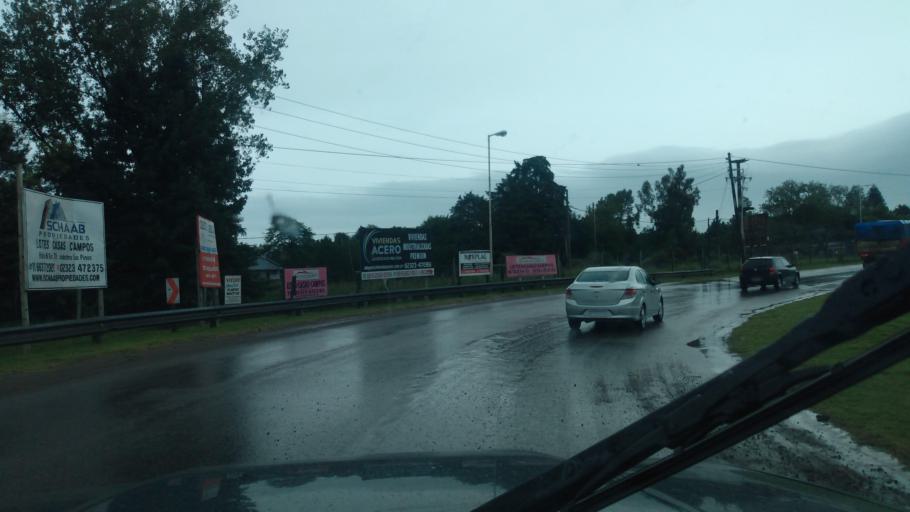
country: AR
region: Buenos Aires
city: Capilla del Senor
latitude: -34.3916
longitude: -59.0346
